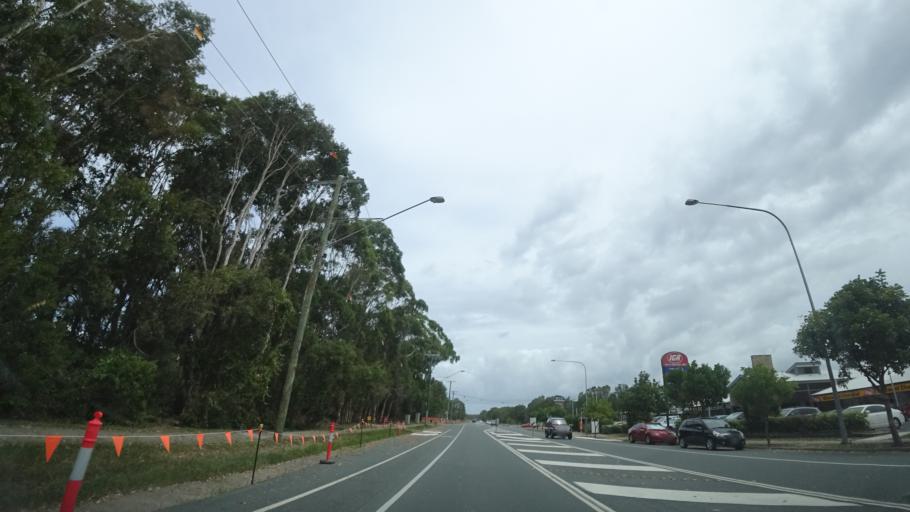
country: AU
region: Queensland
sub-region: Sunshine Coast
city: Coolum Beach
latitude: -26.5654
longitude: 153.0922
